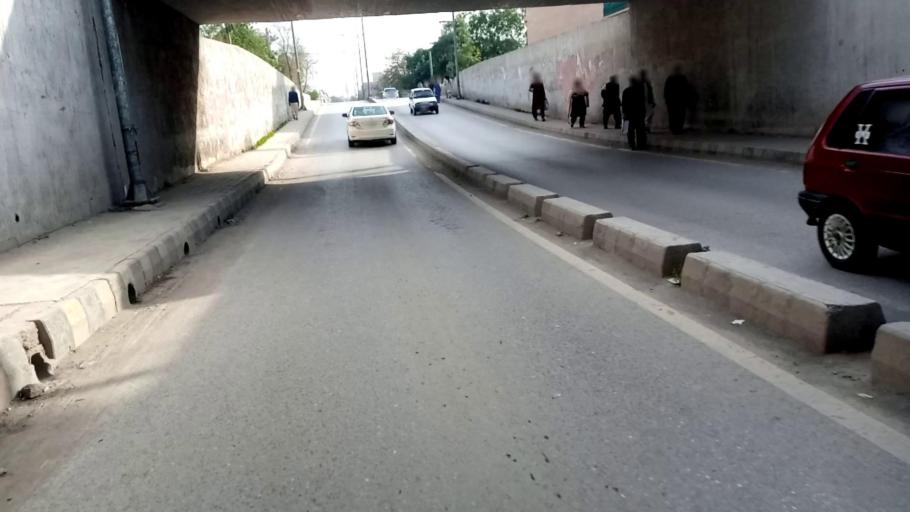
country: PK
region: Khyber Pakhtunkhwa
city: Peshawar
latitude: 33.9963
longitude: 71.4526
